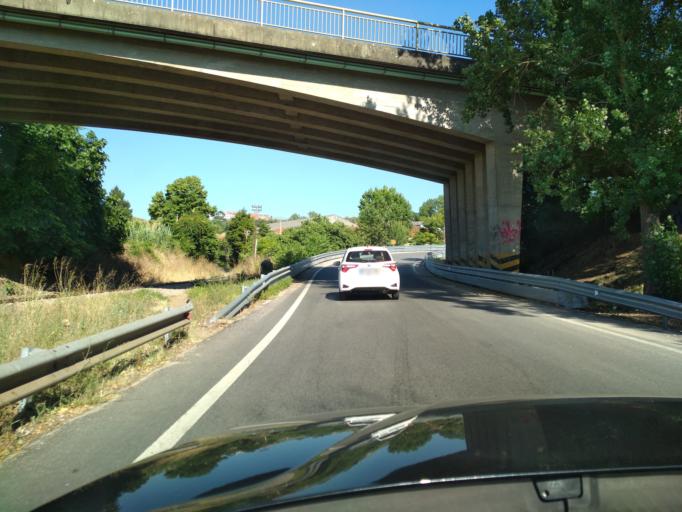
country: PT
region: Coimbra
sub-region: Coimbra
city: Coimbra
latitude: 40.1985
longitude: -8.4213
